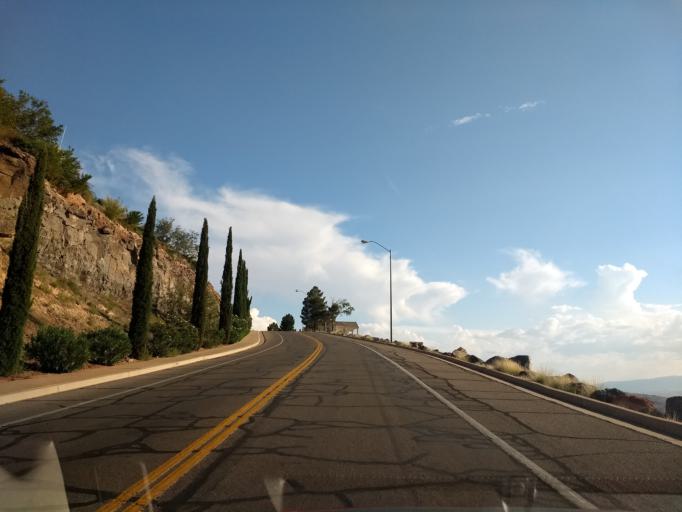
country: US
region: Utah
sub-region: Washington County
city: Saint George
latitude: 37.1125
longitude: -113.5519
